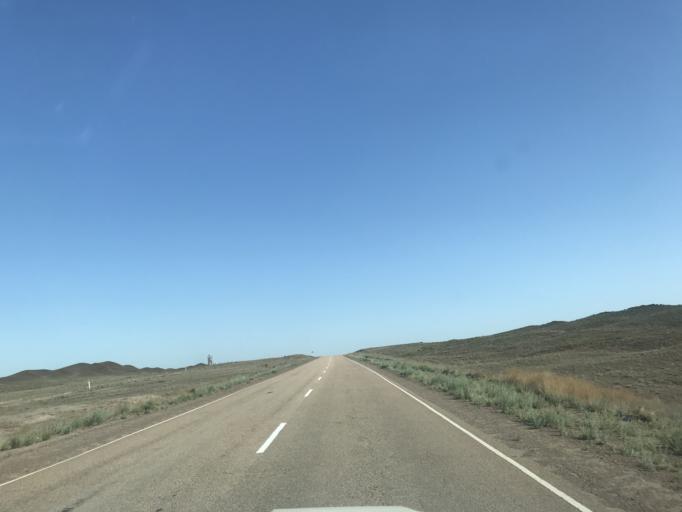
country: KZ
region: Zhambyl
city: Mynaral
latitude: 45.4098
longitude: 73.6307
